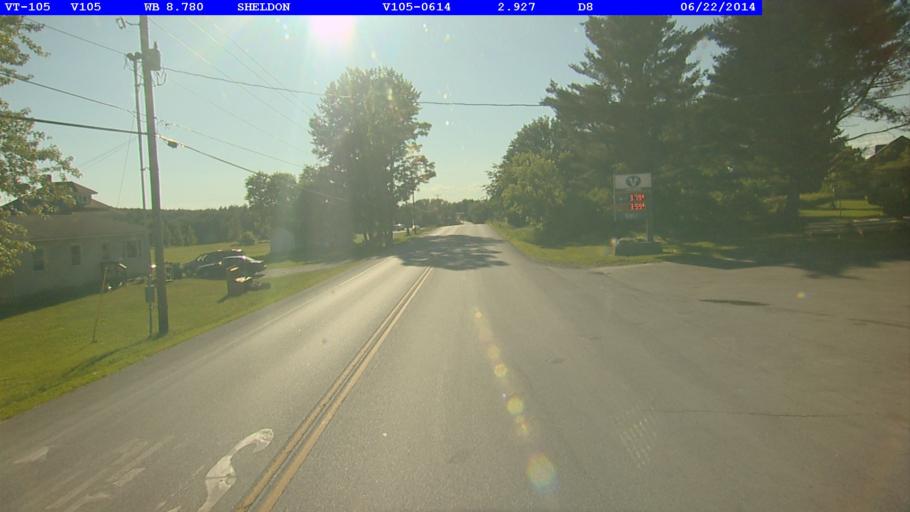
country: US
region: Vermont
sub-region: Franklin County
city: Saint Albans
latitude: 44.9028
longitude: -72.9740
